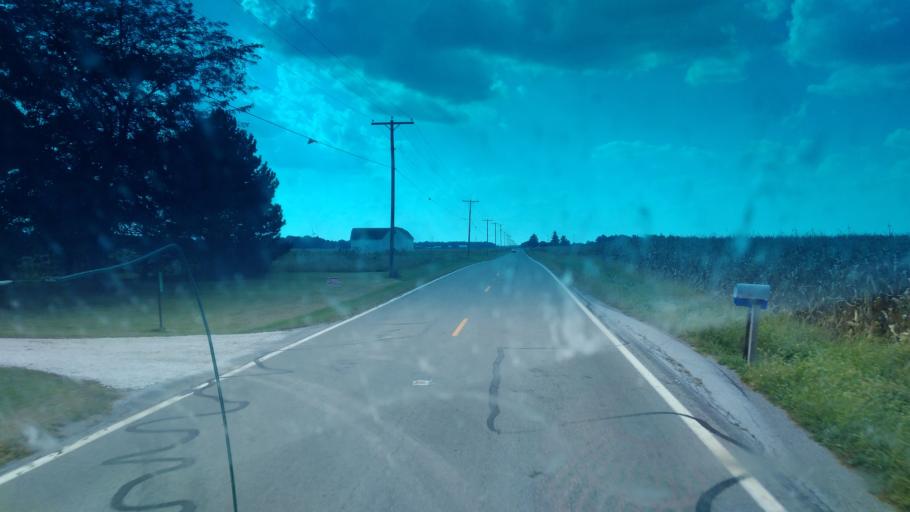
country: US
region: Ohio
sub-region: Hancock County
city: Arlington
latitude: 40.7796
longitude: -83.6652
